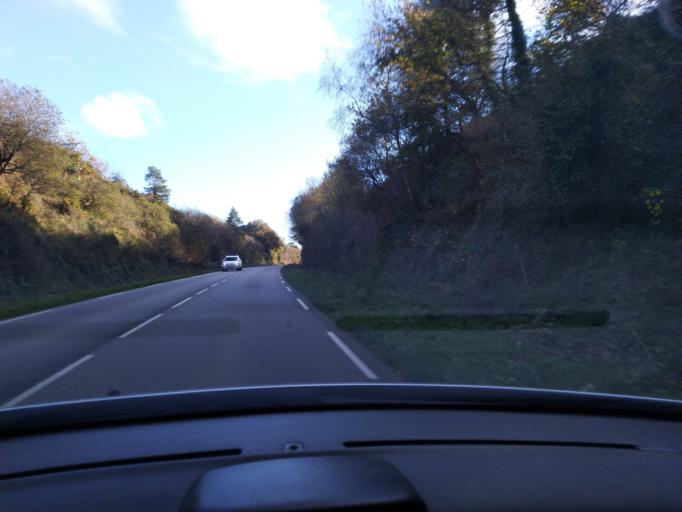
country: FR
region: Brittany
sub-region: Departement du Finistere
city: Guerlesquin
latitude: 48.5608
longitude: -3.6008
